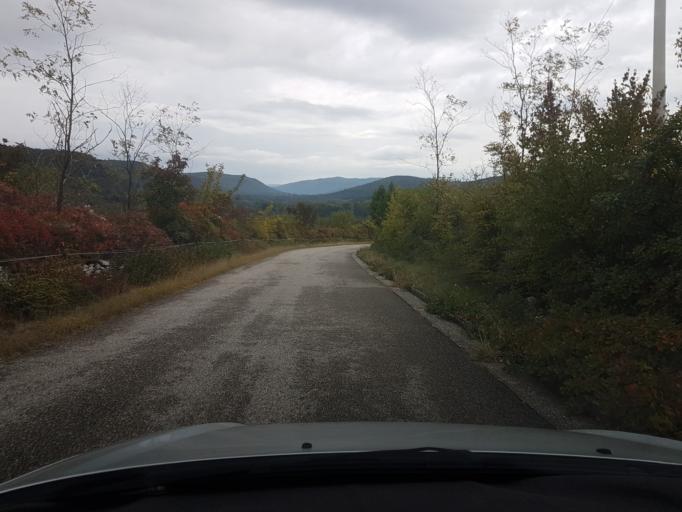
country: IT
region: Friuli Venezia Giulia
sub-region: Provincia di Gorizia
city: Doberdo del Lago
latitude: 45.8386
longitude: 13.5436
